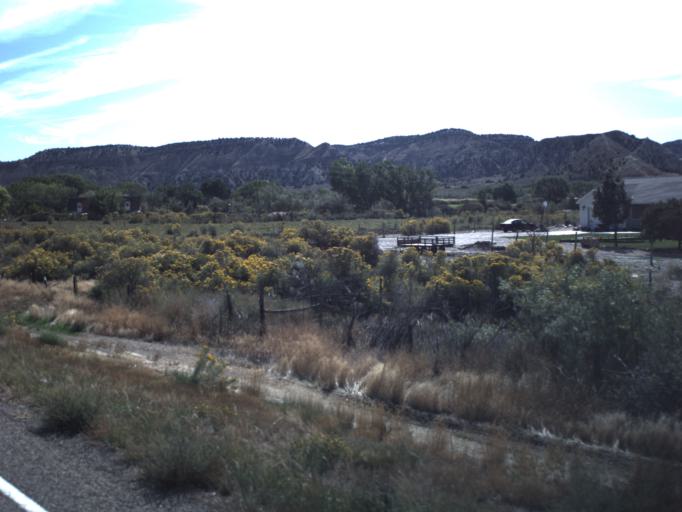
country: US
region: Utah
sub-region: Garfield County
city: Panguitch
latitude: 37.5626
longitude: -112.0046
